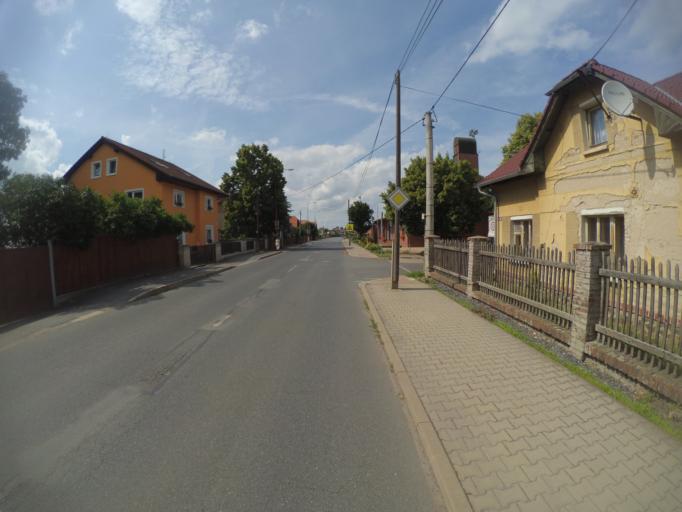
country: CZ
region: Central Bohemia
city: Libis
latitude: 50.2730
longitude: 14.5036
